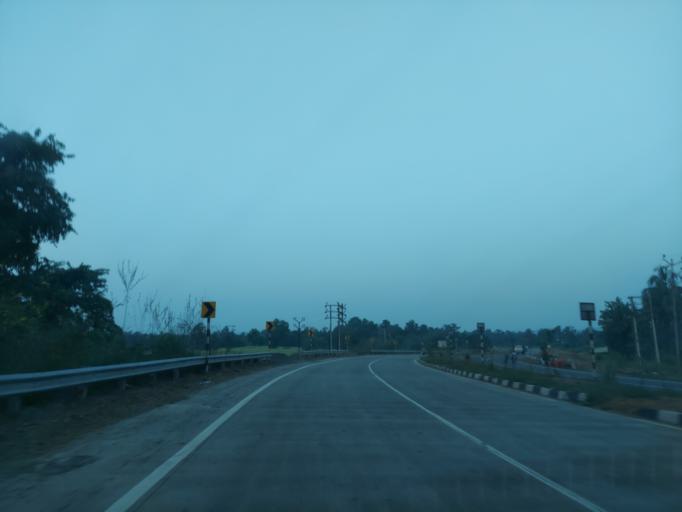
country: IN
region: Maharashtra
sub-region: Sindhudurg
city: Kudal
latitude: 16.0984
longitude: 73.7065
